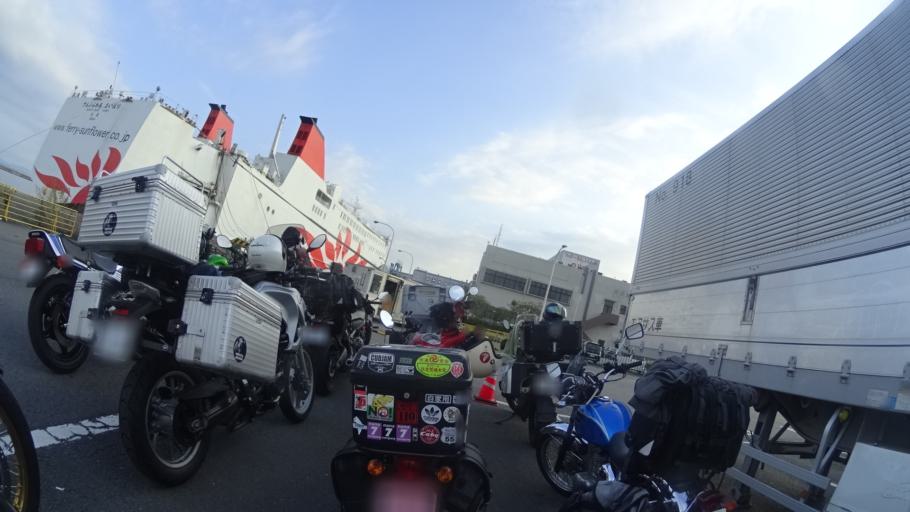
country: JP
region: Oita
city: Beppu
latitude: 33.3041
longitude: 131.5039
